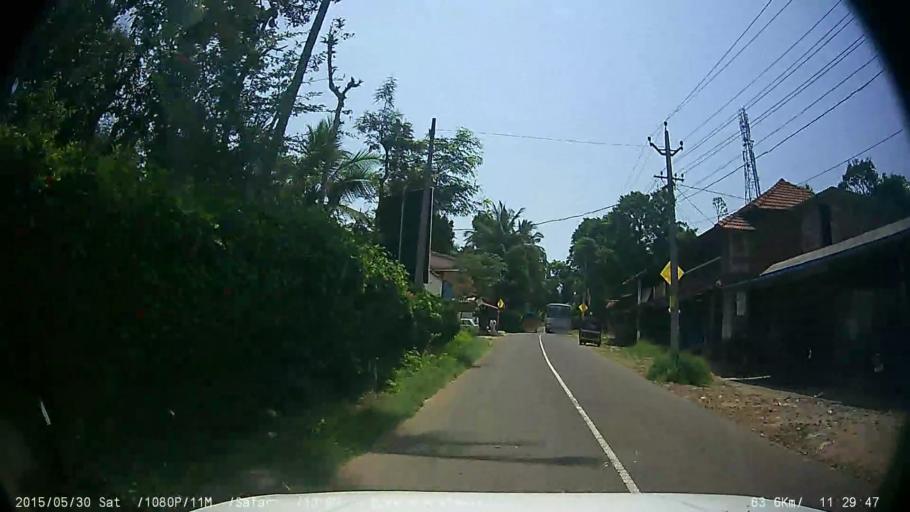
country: IN
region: Kerala
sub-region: Wayanad
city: Panamaram
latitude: 11.8100
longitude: 76.0517
